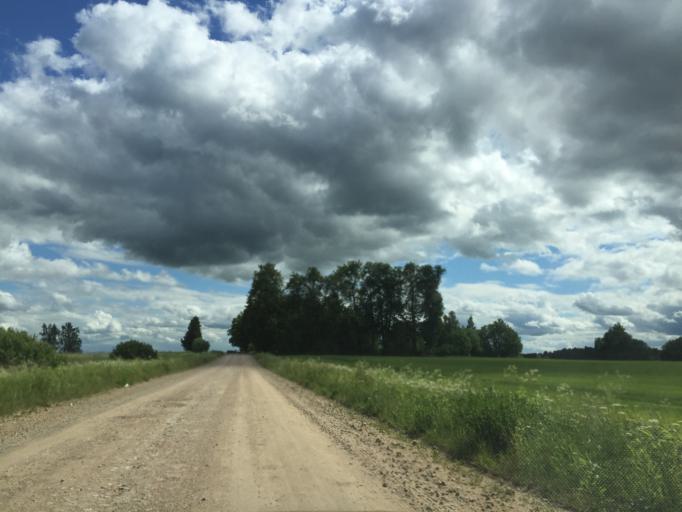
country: LV
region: Vecumnieki
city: Vecumnieki
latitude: 56.4818
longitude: 24.4150
